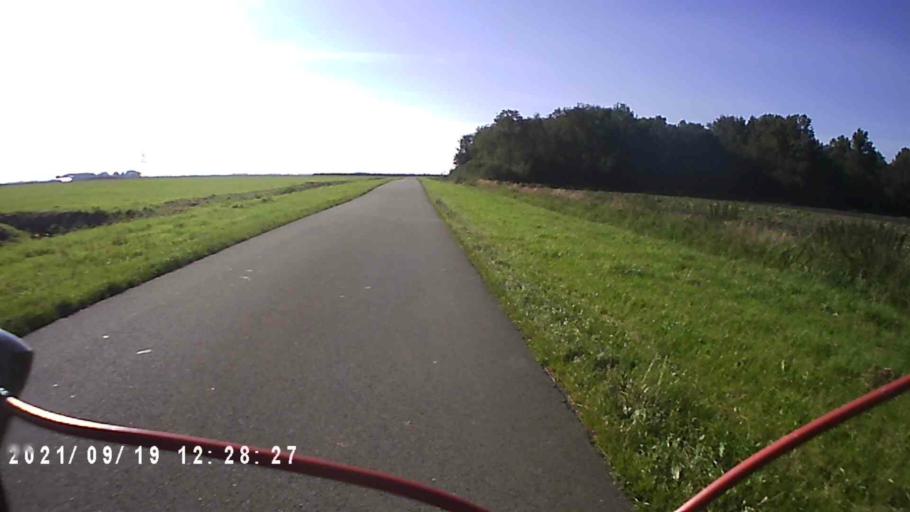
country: NL
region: Groningen
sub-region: Gemeente Slochteren
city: Slochteren
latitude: 53.2271
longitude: 6.8927
